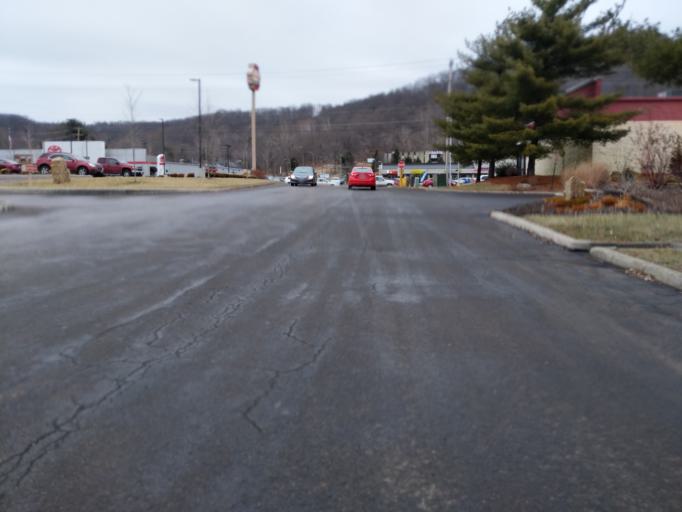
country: US
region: Ohio
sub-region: Athens County
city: Athens
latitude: 39.3363
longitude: -82.0701
